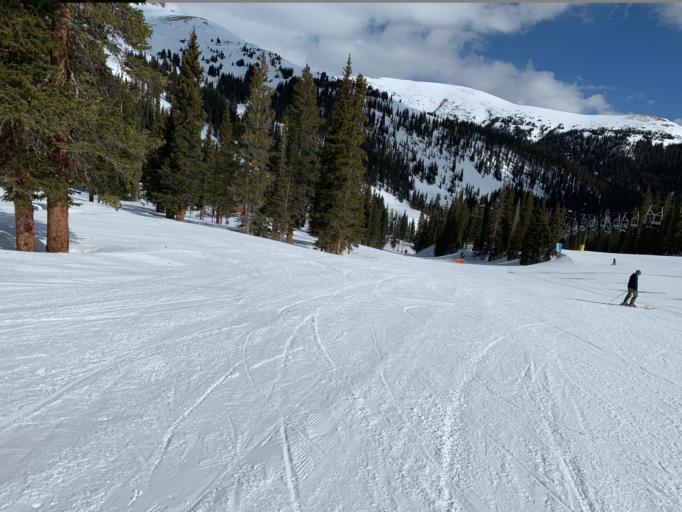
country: US
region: Colorado
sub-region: Summit County
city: Keystone
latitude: 39.6738
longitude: -105.9053
